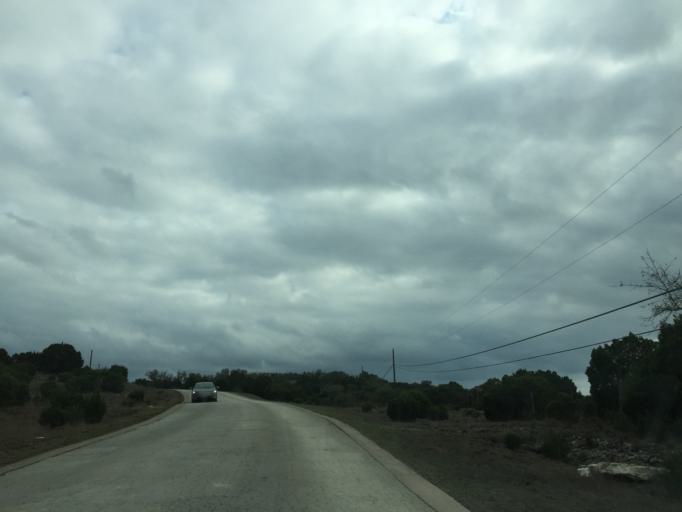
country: US
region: Texas
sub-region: Travis County
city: Shady Hollow
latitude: 30.1486
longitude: -97.9722
